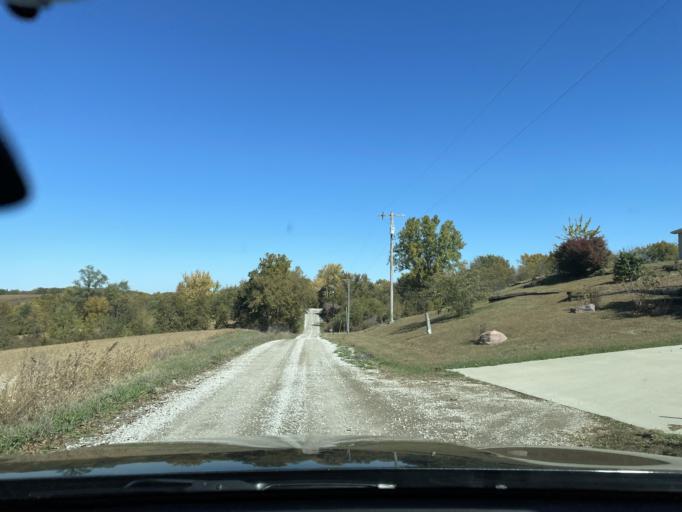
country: US
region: Missouri
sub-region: Andrew County
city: Savannah
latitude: 39.9339
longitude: -94.8804
